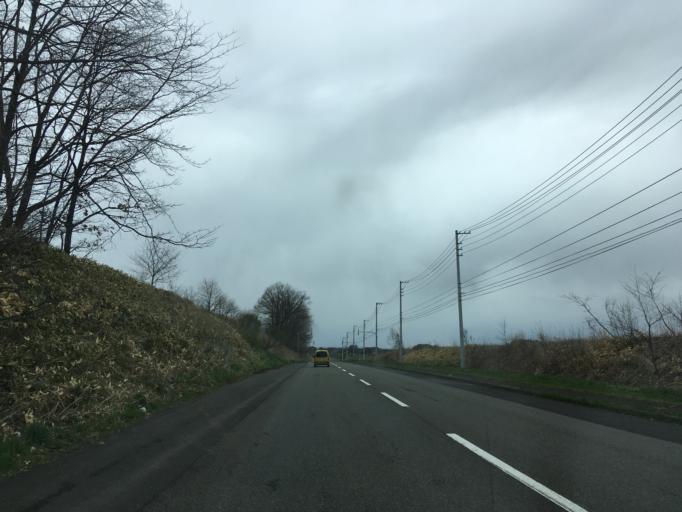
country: JP
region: Hokkaido
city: Chitose
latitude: 42.9013
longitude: 141.8134
